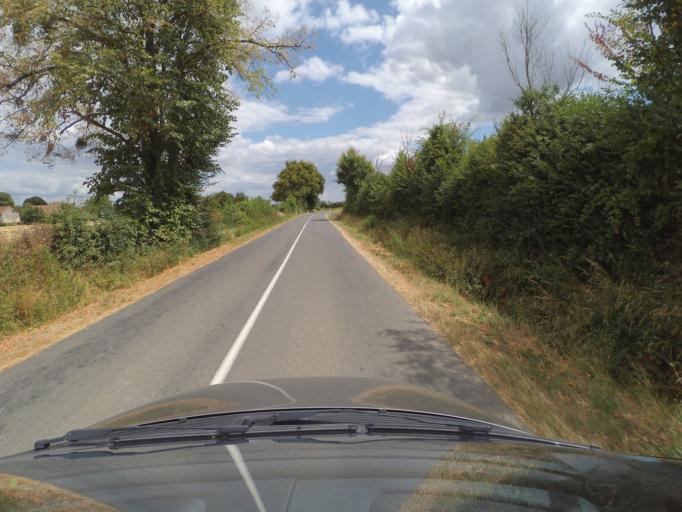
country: FR
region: Poitou-Charentes
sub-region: Departement de la Vienne
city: Saint-Savin
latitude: 46.5592
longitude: 0.9371
